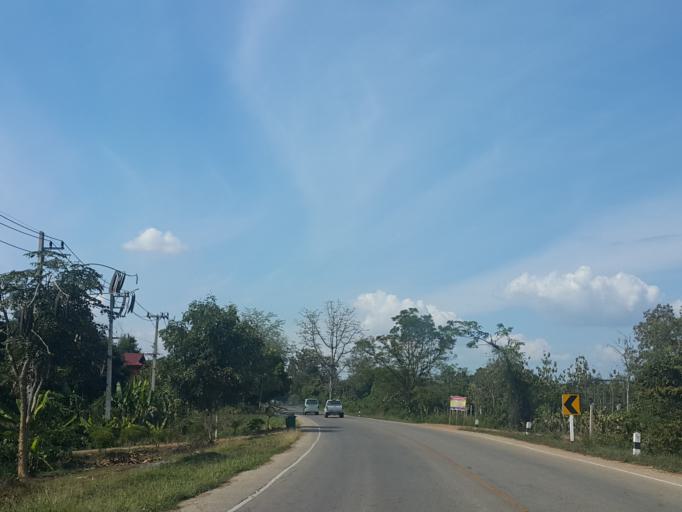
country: TH
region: Sukhothai
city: Sawankhalok
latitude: 17.2501
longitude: 99.8459
